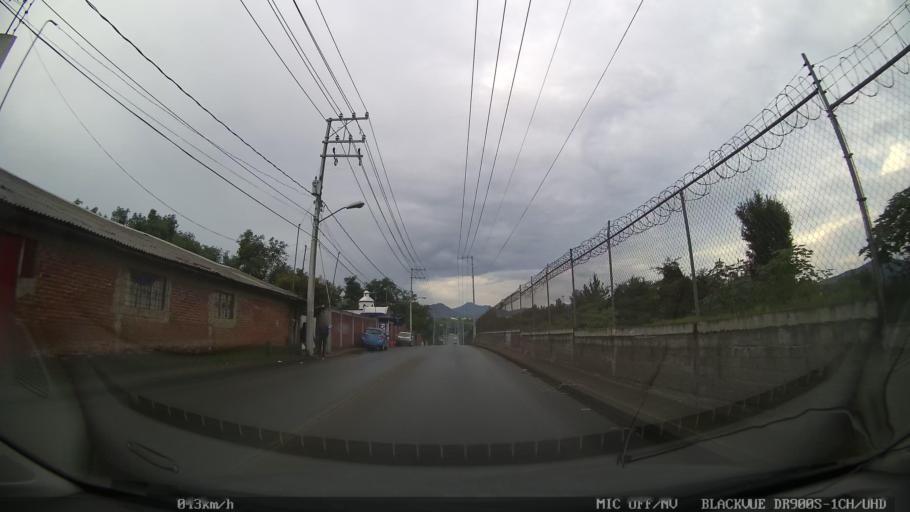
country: MX
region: Michoacan
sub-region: Uruapan
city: Santa Rosa (Santa Barbara)
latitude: 19.3826
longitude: -102.0459
